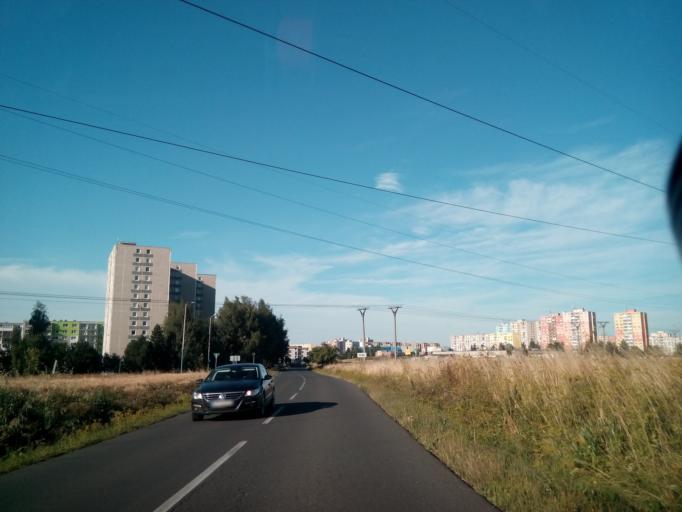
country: SK
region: Presovsky
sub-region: Okres Poprad
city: Poprad
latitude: 49.0416
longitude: 20.2850
